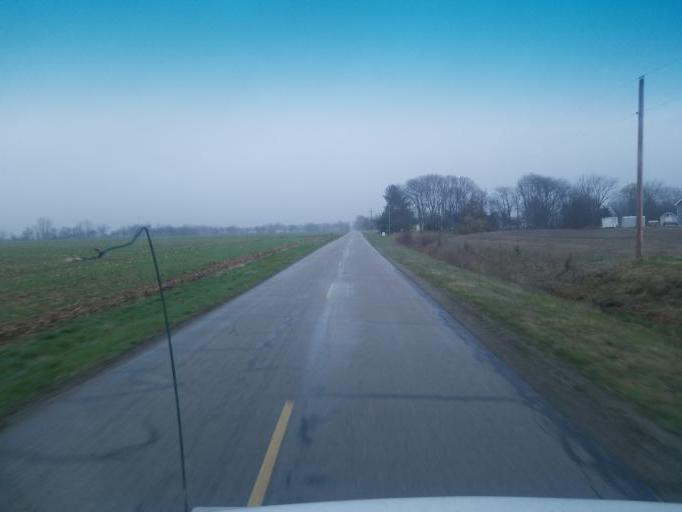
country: US
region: Ohio
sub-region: Henry County
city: Napoleon
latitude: 41.4135
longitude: -84.2011
